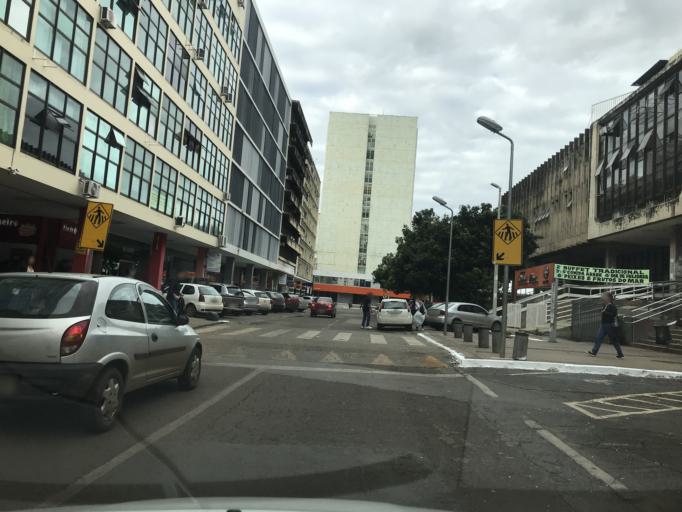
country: BR
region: Federal District
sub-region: Brasilia
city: Brasilia
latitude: -15.7978
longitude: -47.8876
